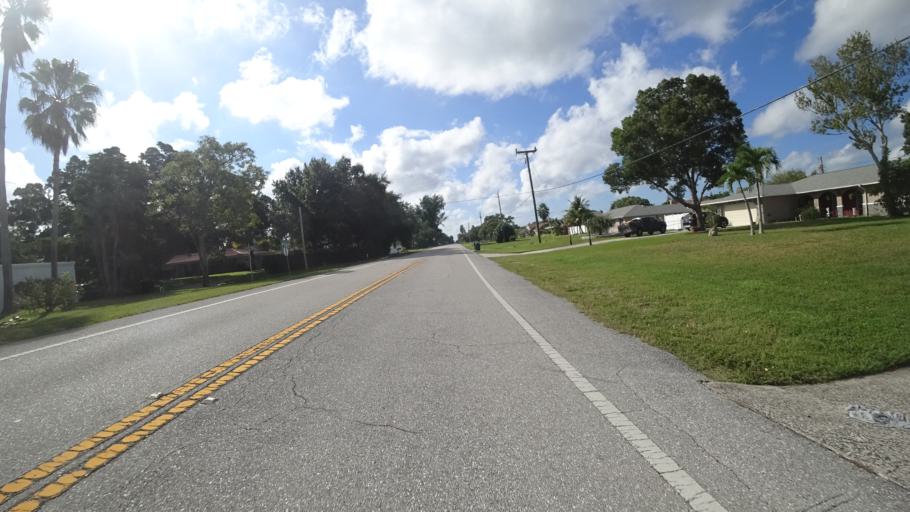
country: US
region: Florida
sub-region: Manatee County
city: West Bradenton
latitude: 27.5165
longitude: -82.6365
